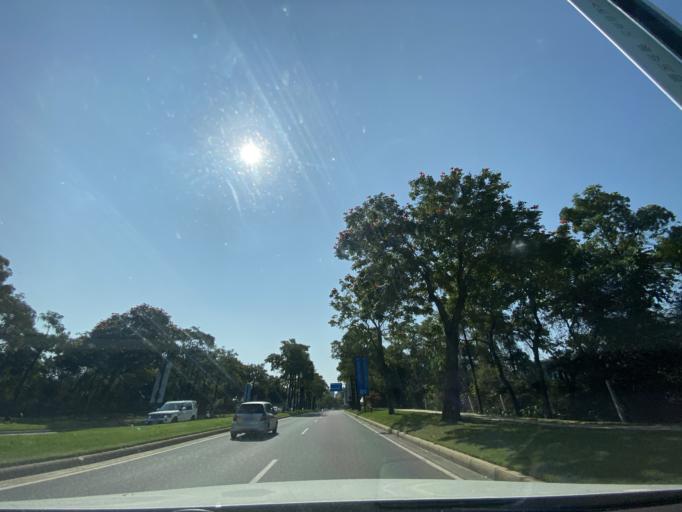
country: CN
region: Hainan
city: Yingzhou
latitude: 18.4091
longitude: 109.8472
